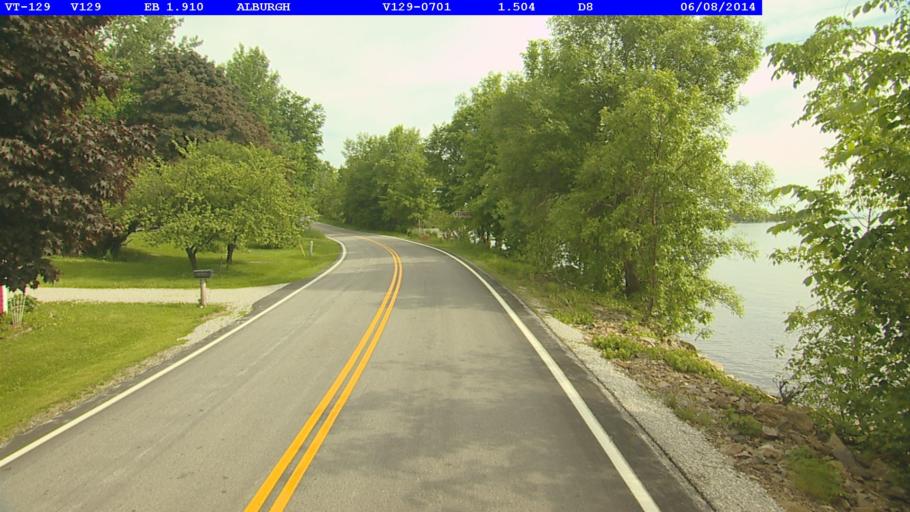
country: US
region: Vermont
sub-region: Grand Isle County
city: North Hero
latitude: 44.8894
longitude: -73.3036
